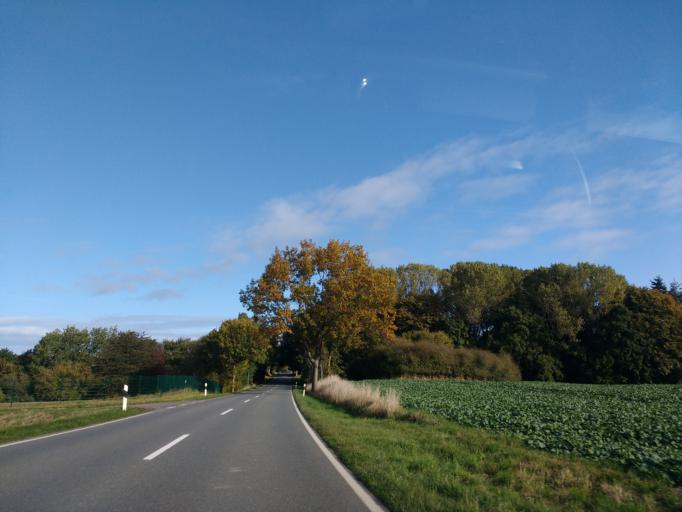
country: DE
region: Schleswig-Holstein
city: Wangels
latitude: 54.2484
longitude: 10.7463
